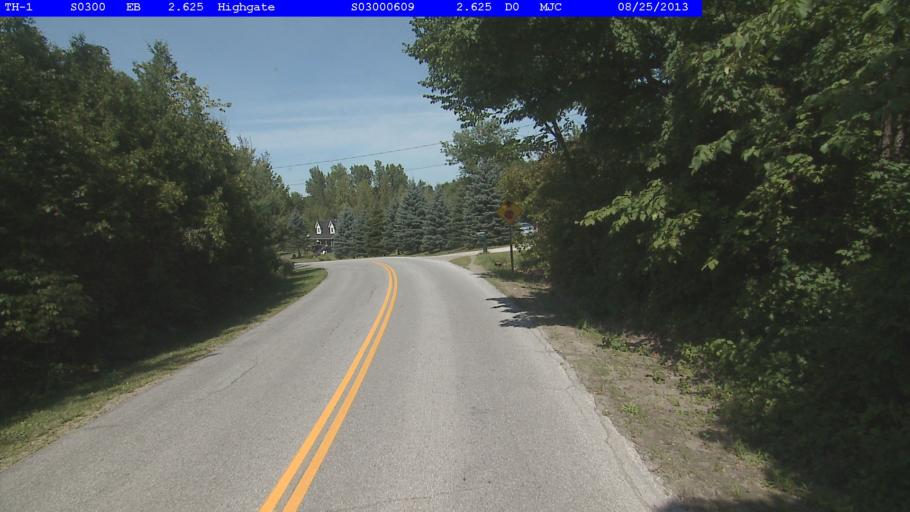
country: US
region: Vermont
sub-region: Franklin County
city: Swanton
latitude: 44.9612
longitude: -73.0944
